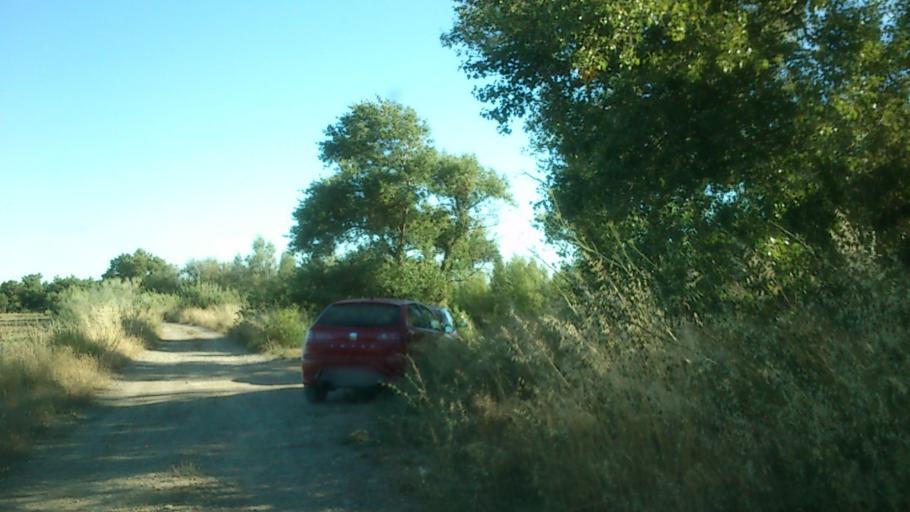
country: ES
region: Aragon
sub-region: Provincia de Zaragoza
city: Villanueva de Gallego
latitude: 41.7687
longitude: -0.8067
